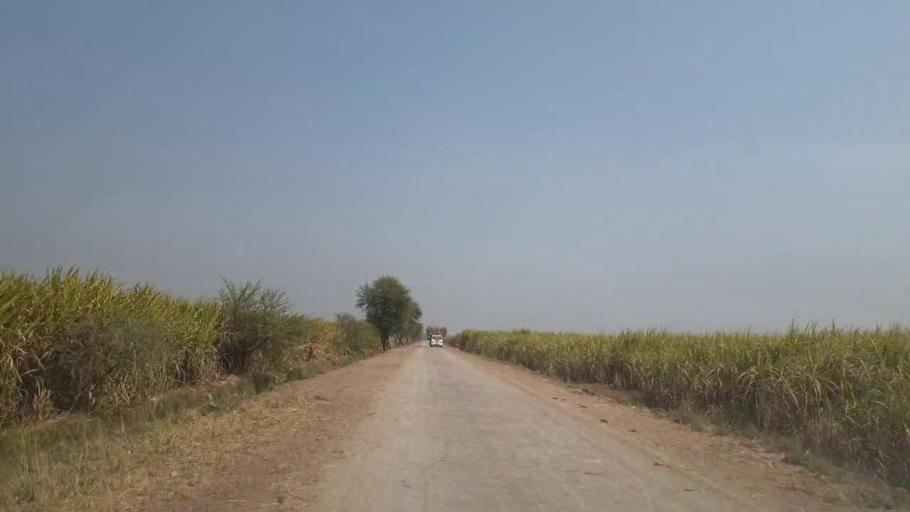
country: PK
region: Sindh
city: Mirpur Khas
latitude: 25.5443
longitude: 69.0842
